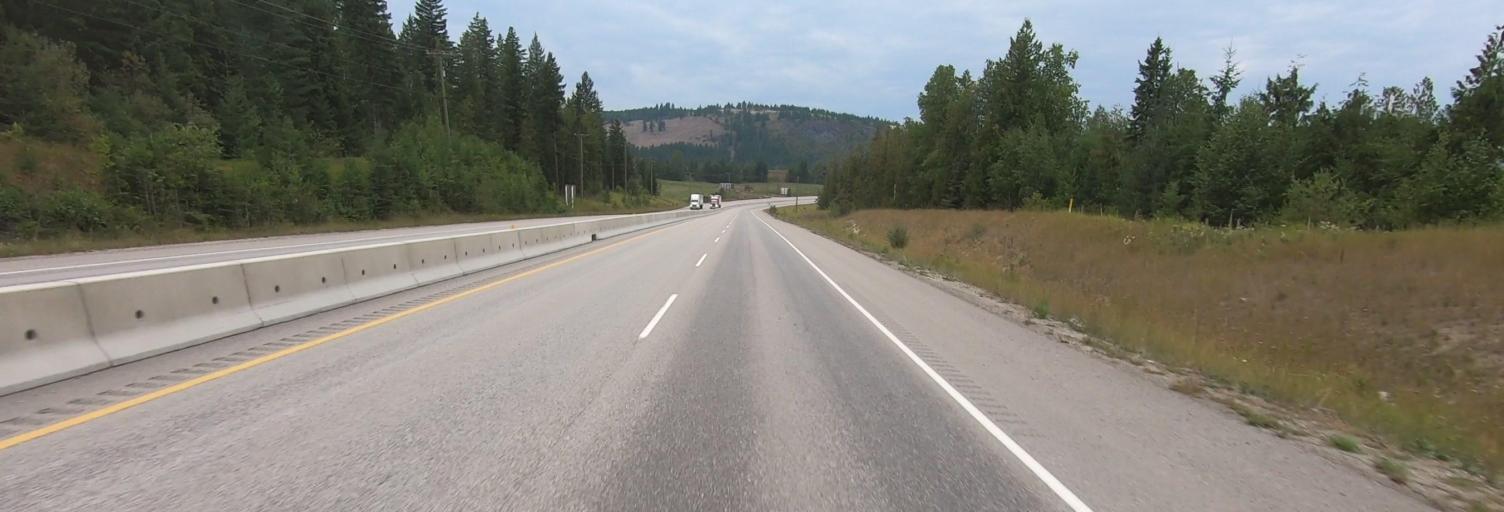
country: CA
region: British Columbia
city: Salmon Arm
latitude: 50.8545
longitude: -119.3616
